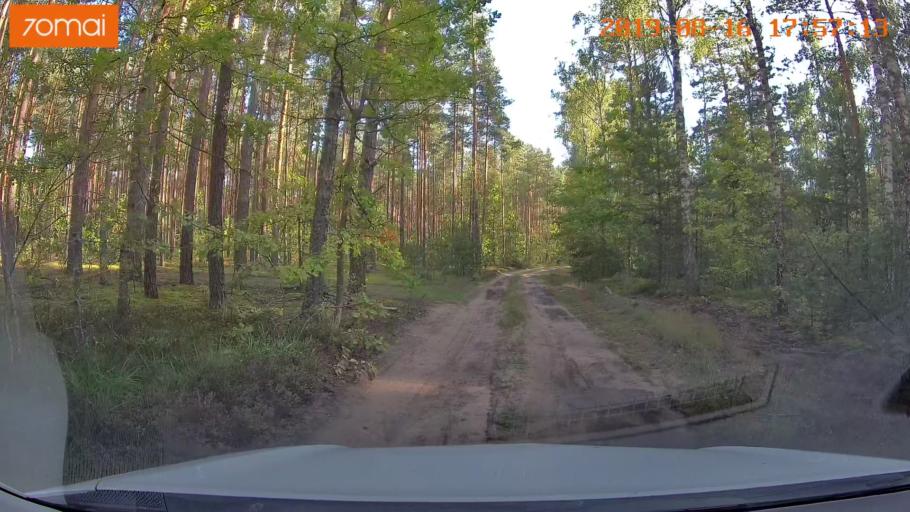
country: BY
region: Mogilev
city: Asipovichy
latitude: 53.2240
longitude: 28.6589
